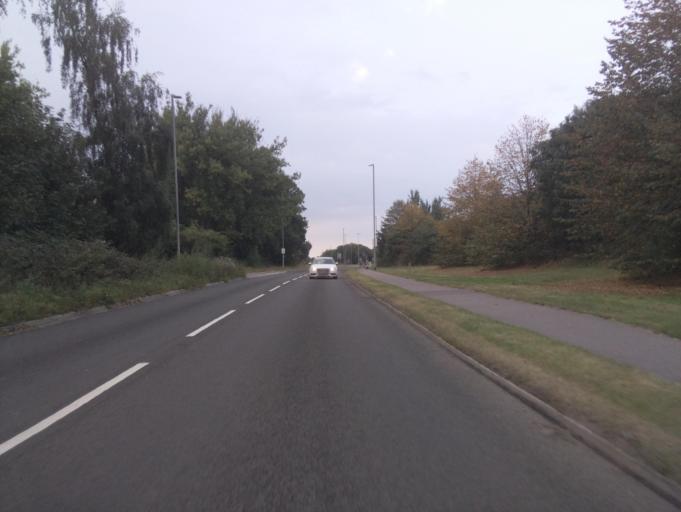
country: GB
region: England
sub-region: Nottinghamshire
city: South Collingham
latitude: 53.1470
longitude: -0.6692
